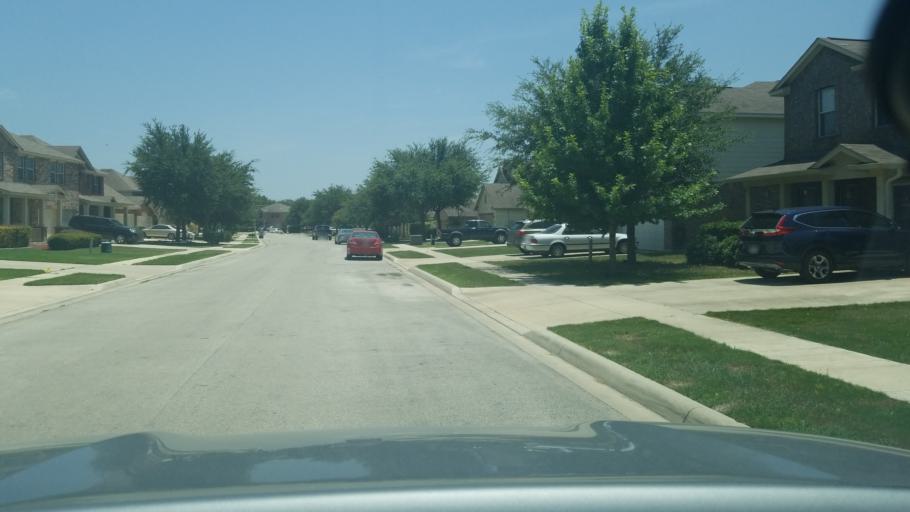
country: US
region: Texas
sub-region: Guadalupe County
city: Cibolo
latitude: 29.5755
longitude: -98.2296
